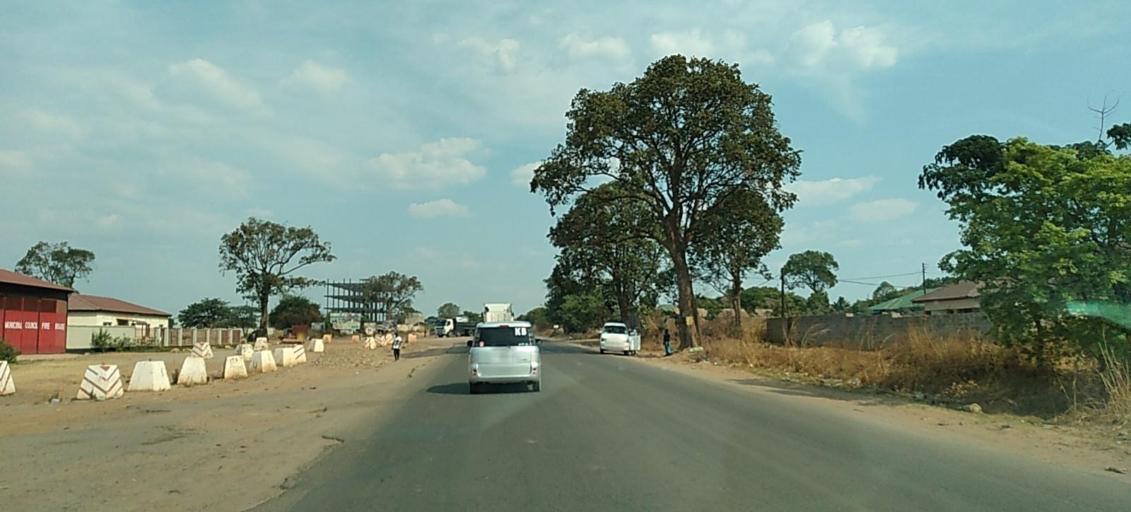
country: ZM
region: Copperbelt
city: Chililabombwe
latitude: -12.3616
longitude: 27.8501
